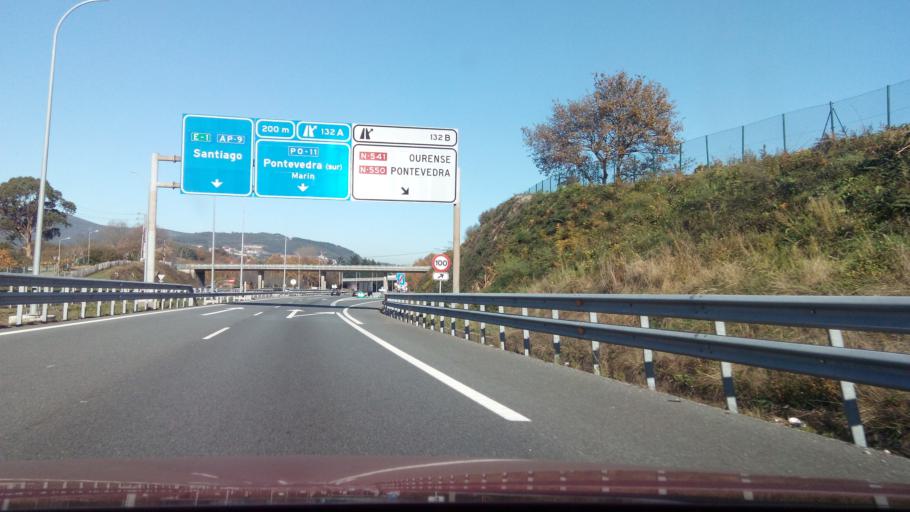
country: ES
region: Galicia
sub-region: Provincia de Pontevedra
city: Poio
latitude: 42.4097
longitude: -8.6536
